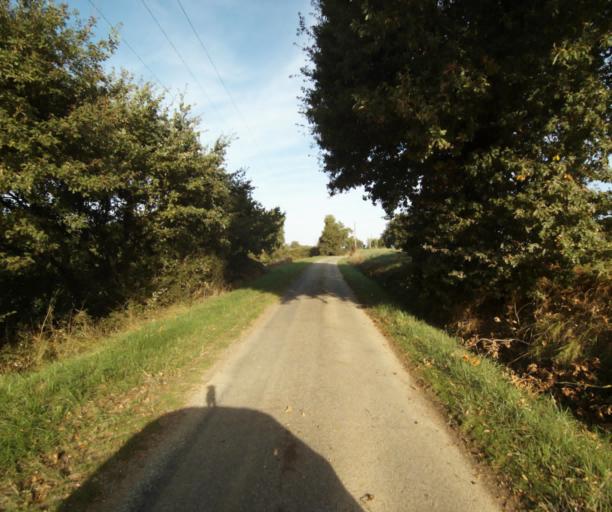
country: FR
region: Midi-Pyrenees
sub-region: Departement de la Haute-Garonne
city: Villemur-sur-Tarn
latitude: 43.9055
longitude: 1.5022
